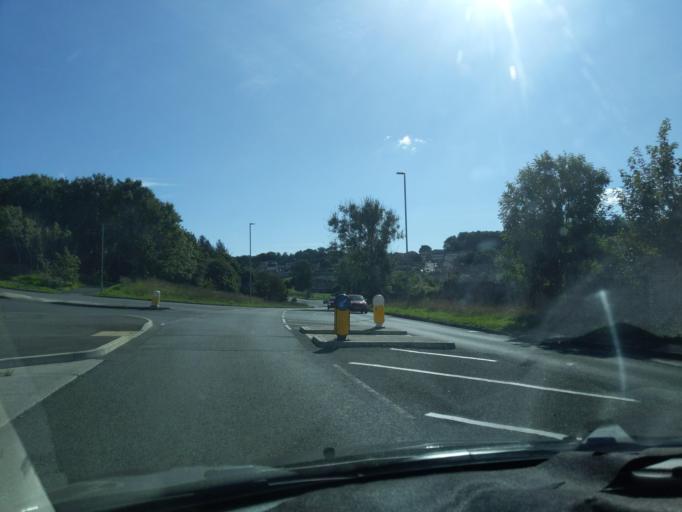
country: GB
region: England
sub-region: Devon
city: Plympton
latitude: 50.3876
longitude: -4.0324
